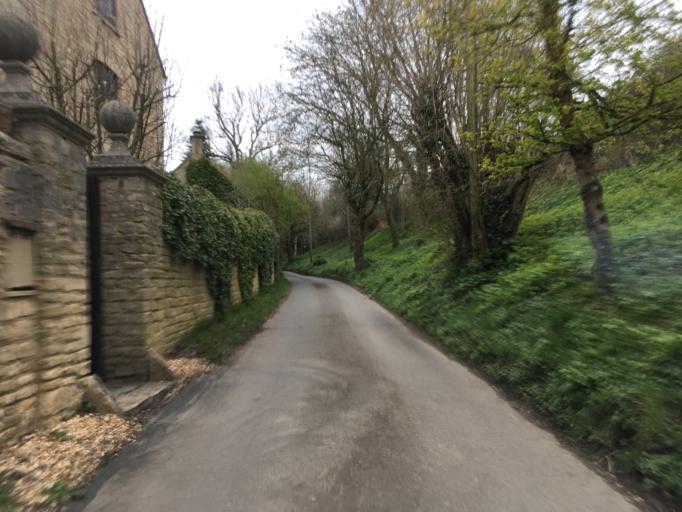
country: GB
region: England
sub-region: Gloucestershire
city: Wotton-under-Edge
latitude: 51.5992
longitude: -2.3075
